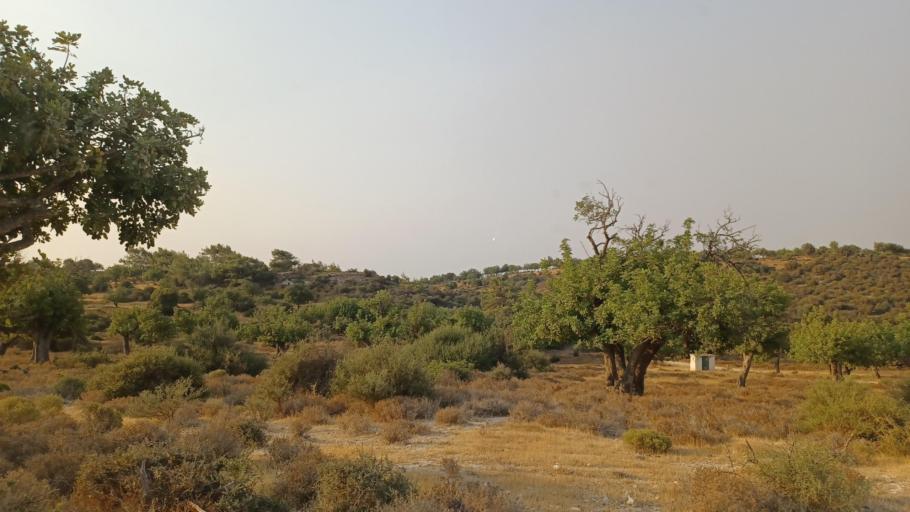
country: CY
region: Limassol
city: Pissouri
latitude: 34.6960
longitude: 32.6556
